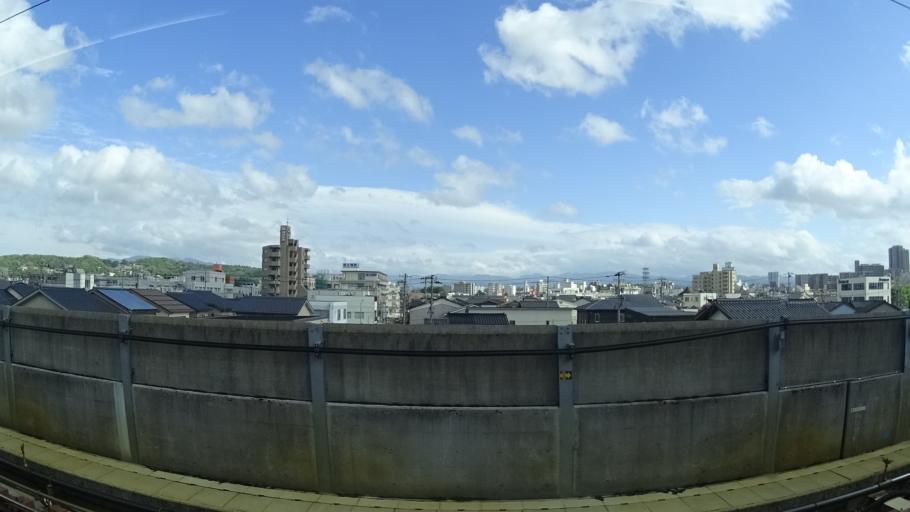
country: JP
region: Ishikawa
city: Kanazawa-shi
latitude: 36.5836
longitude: 136.6549
